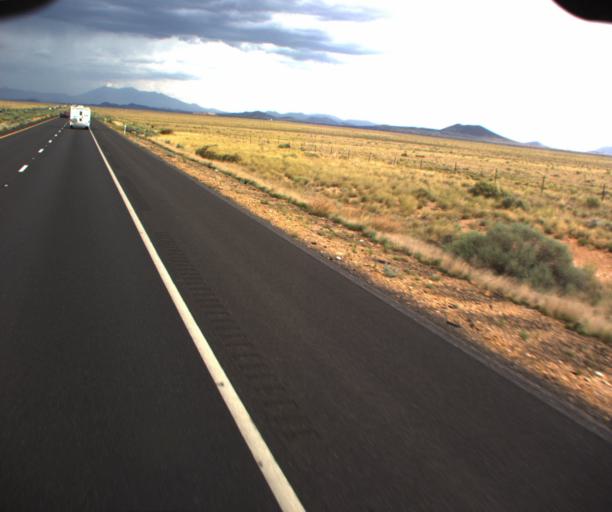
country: US
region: Arizona
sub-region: Coconino County
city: Flagstaff
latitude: 35.1378
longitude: -111.2071
